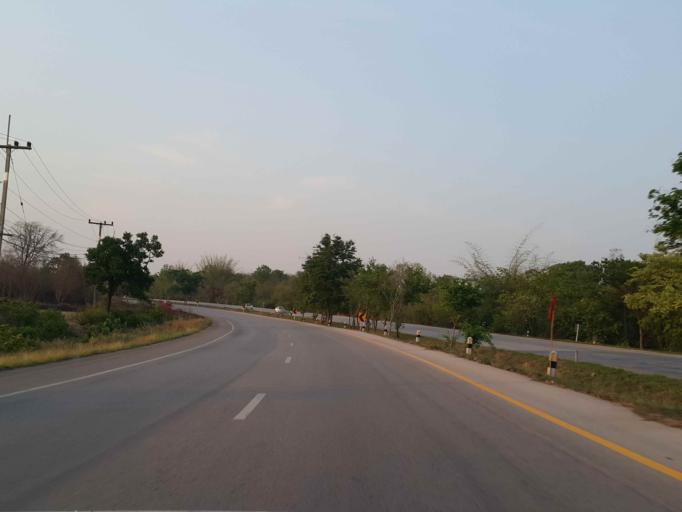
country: TH
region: Lampang
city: Sop Prap
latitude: 17.9586
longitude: 99.3541
